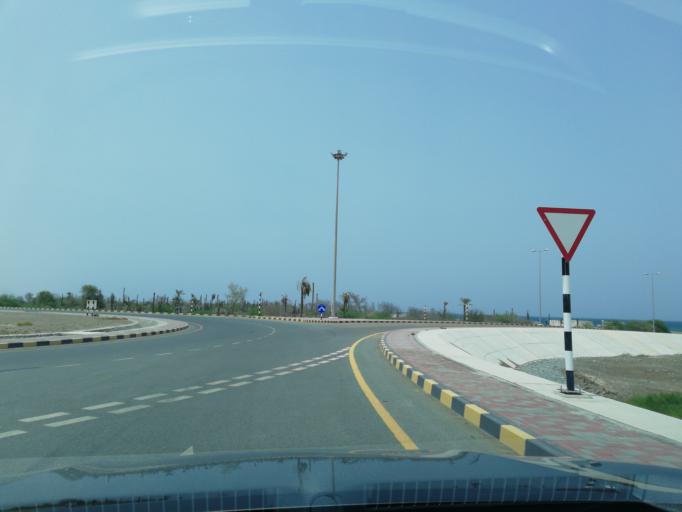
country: OM
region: Al Batinah
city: Al Liwa'
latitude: 24.6411
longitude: 56.5208
